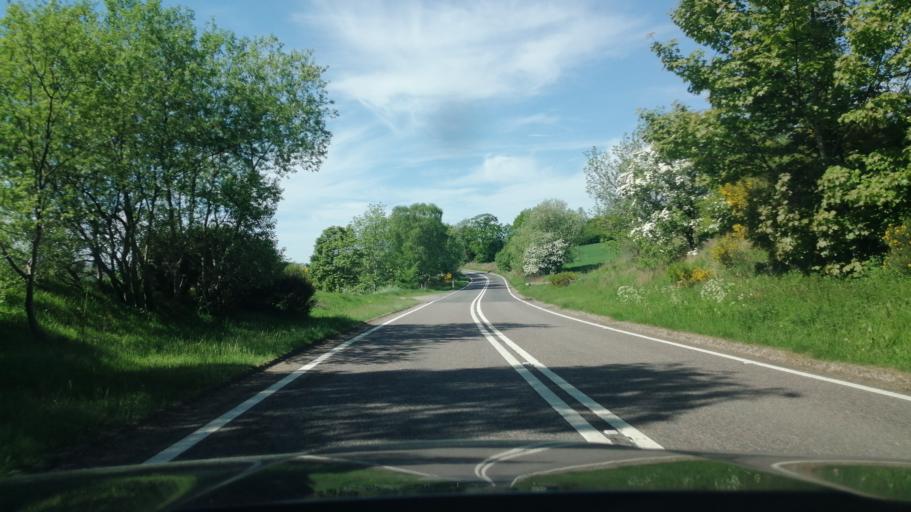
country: GB
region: Scotland
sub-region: Moray
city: Dufftown
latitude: 57.4939
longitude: -3.1508
